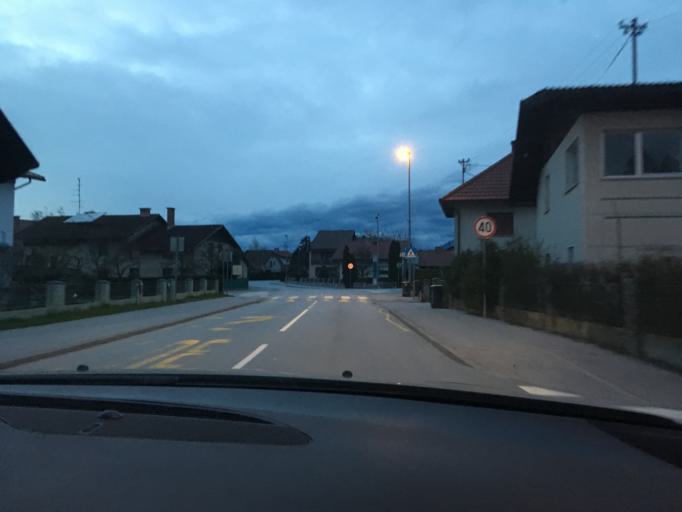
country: SI
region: Domzale
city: Vir
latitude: 46.1483
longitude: 14.6069
